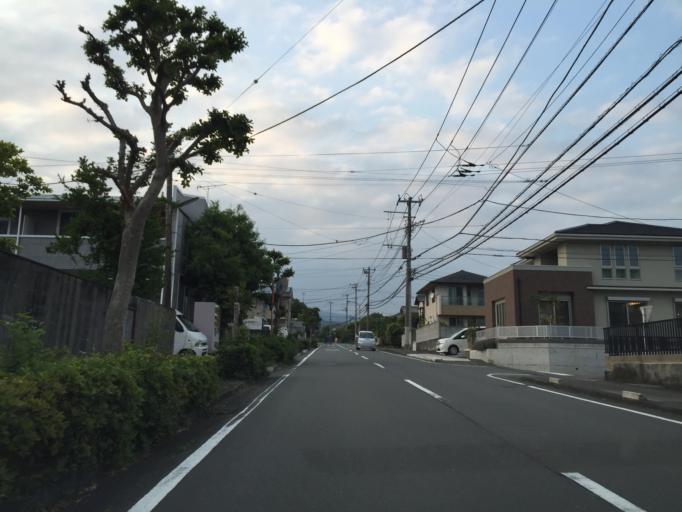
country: JP
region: Shizuoka
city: Numazu
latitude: 35.1330
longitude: 138.8586
